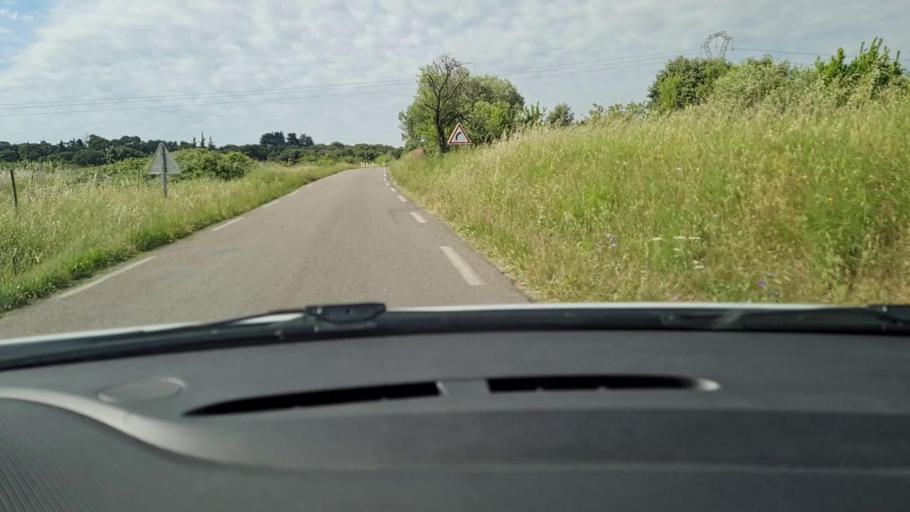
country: FR
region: Languedoc-Roussillon
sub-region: Departement du Gard
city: Jonquieres-Saint-Vincent
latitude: 43.8193
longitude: 4.5569
